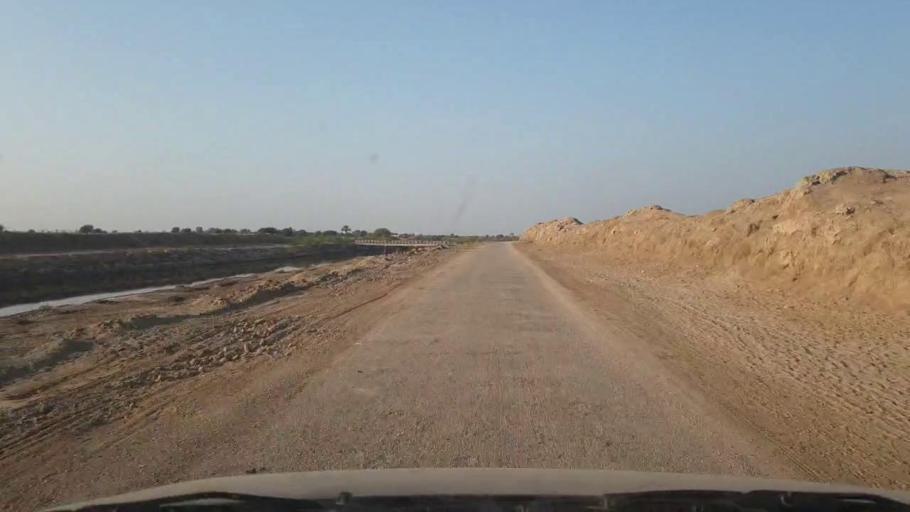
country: PK
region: Sindh
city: Samaro
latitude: 25.2962
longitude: 69.3310
